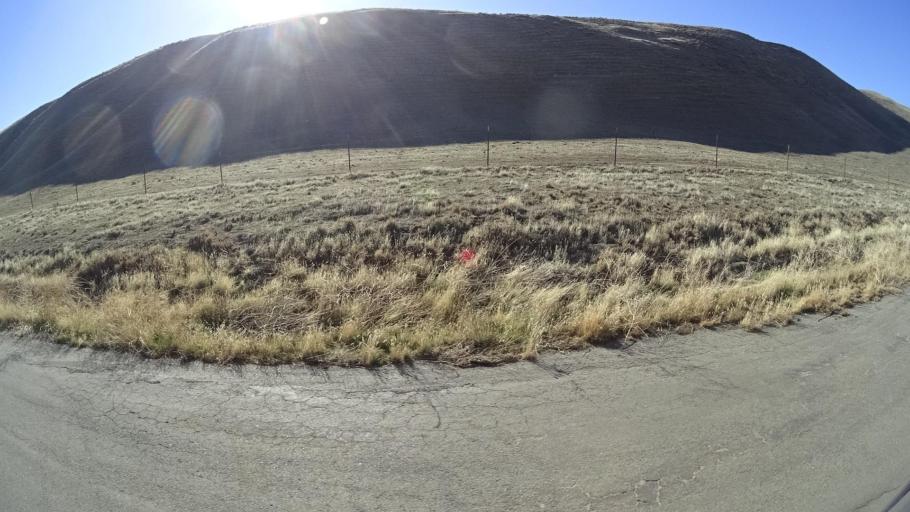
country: US
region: California
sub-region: Kern County
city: Maricopa
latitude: 34.9782
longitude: -119.4647
